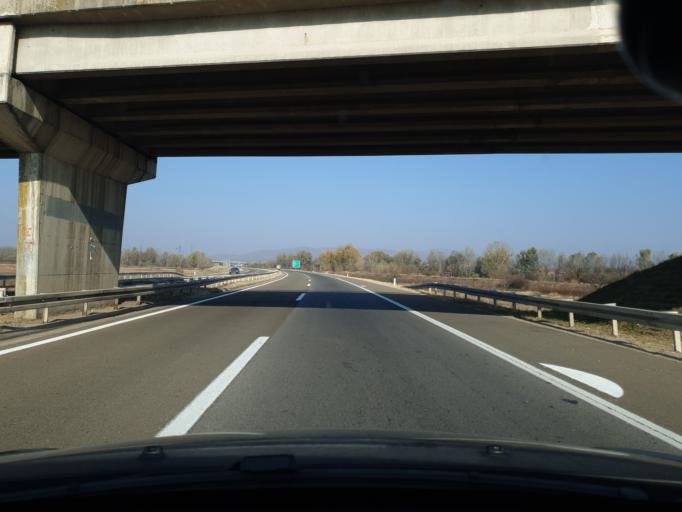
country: RS
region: Central Serbia
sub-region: Nisavski Okrug
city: Nis
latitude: 43.3333
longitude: 21.8145
